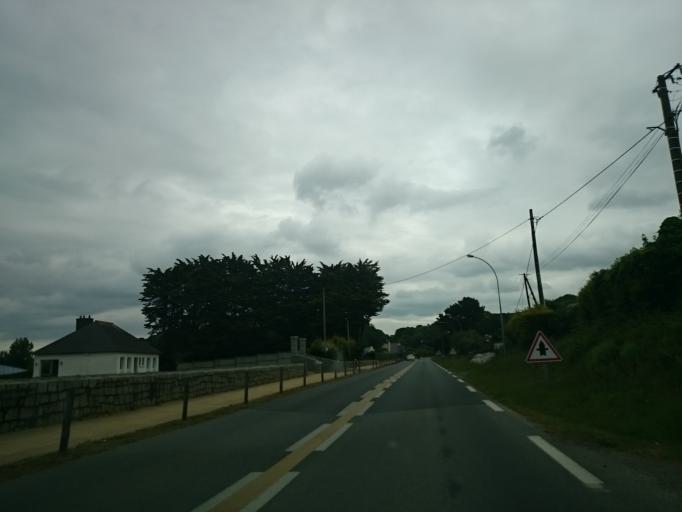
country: FR
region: Brittany
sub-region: Departement des Cotes-d'Armor
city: Louannec
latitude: 48.7970
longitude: -3.4301
